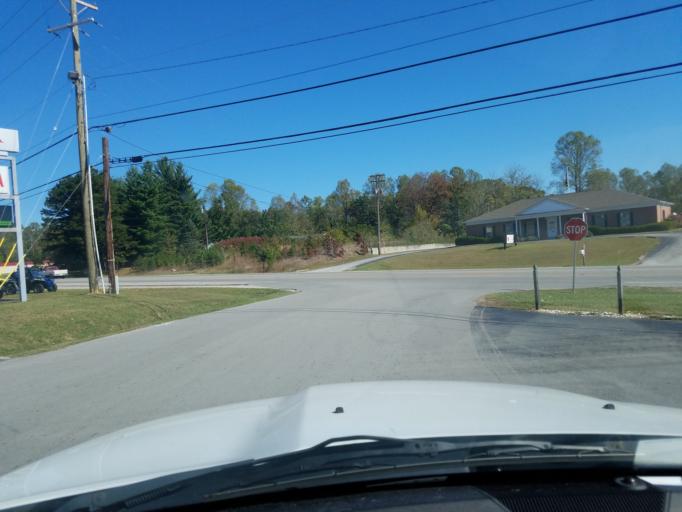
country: US
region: Kentucky
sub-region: Laurel County
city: North Corbin
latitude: 36.9886
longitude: -84.0806
